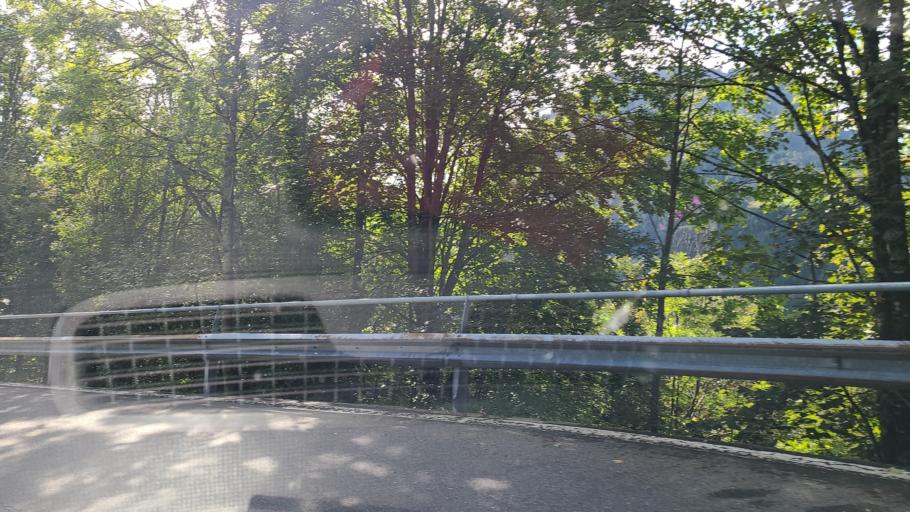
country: CH
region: Schwyz
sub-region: Bezirk March
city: Vorderthal
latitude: 47.1318
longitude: 8.8768
